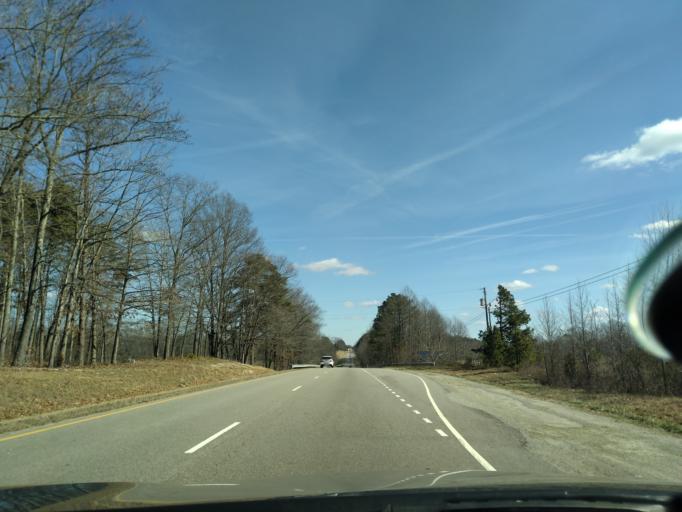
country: US
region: Virginia
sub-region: Nottoway County
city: Crewe
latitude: 37.1897
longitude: -78.1707
